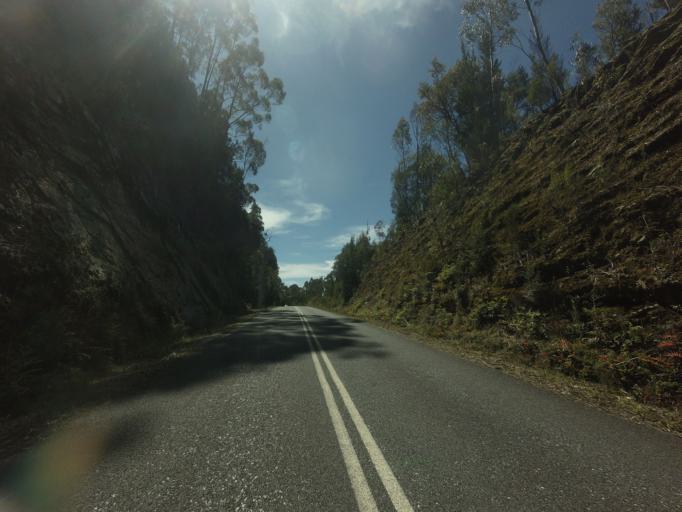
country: AU
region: Tasmania
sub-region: West Coast
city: Queenstown
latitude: -42.7656
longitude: 146.0053
